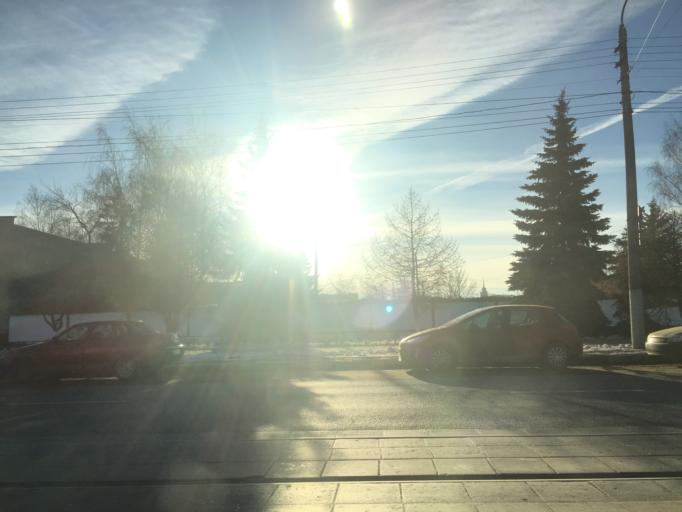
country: RU
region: Tula
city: Tula
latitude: 54.2012
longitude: 37.6292
